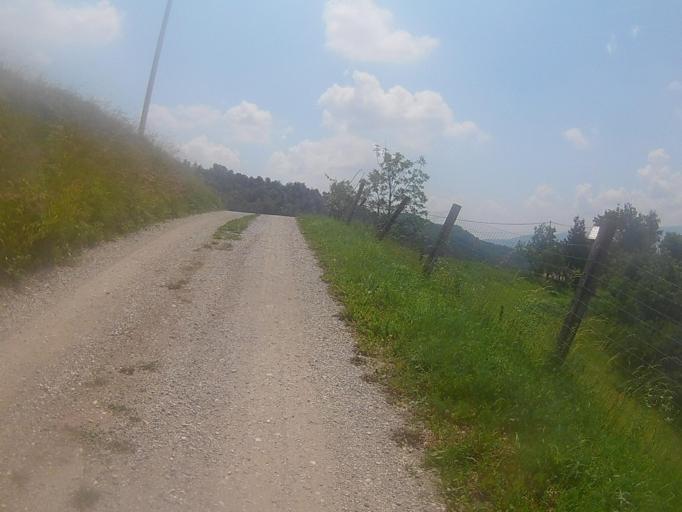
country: SI
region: Maribor
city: Kamnica
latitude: 46.5965
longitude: 15.5997
